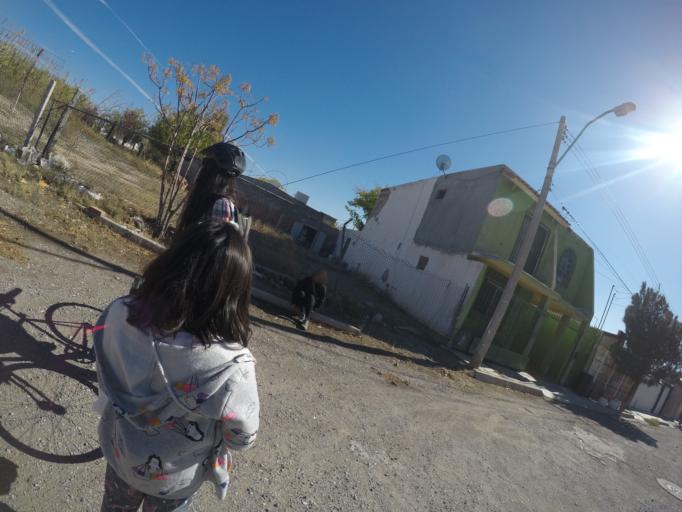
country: MX
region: Chihuahua
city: Ciudad Juarez
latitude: 31.7299
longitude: -106.4302
